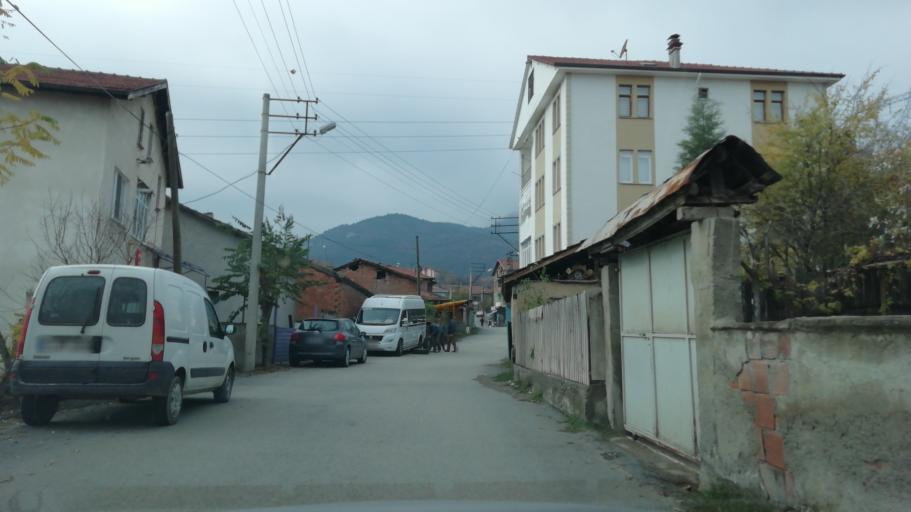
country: TR
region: Karabuk
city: Karabuk
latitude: 41.2299
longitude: 32.6235
